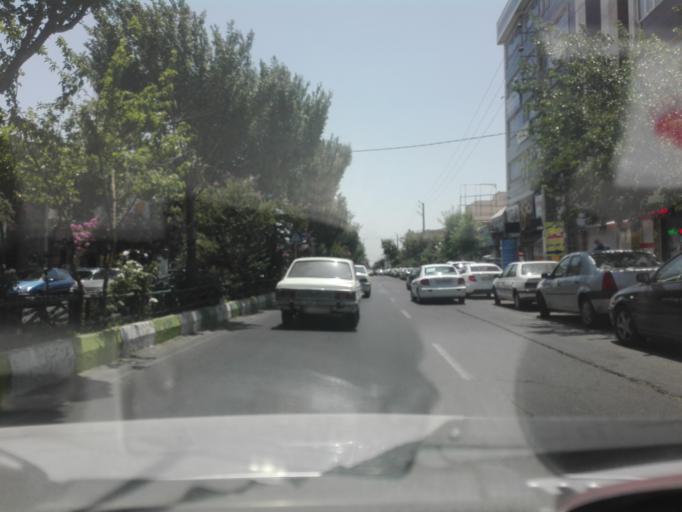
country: IR
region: Tehran
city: Shahre Jadide Andisheh
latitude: 35.7343
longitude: 50.9909
